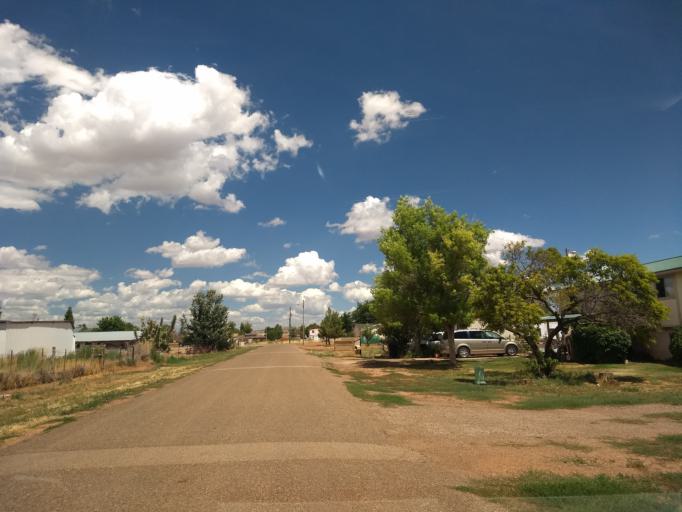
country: US
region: Arizona
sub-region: Coconino County
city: Fredonia
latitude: 36.9444
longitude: -112.5205
